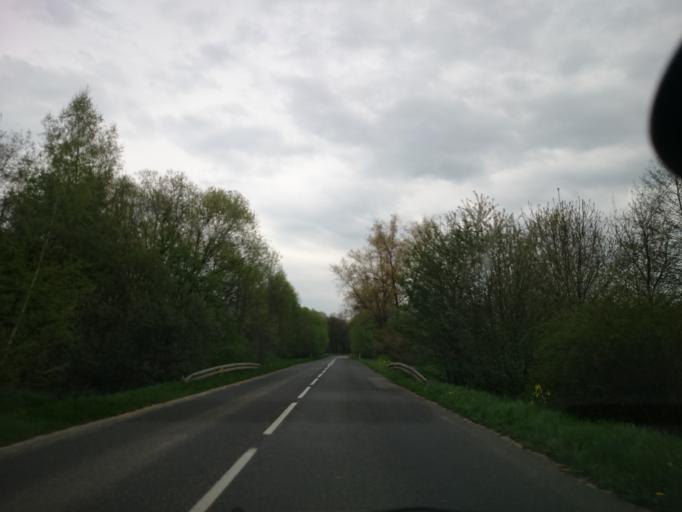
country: PL
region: Opole Voivodeship
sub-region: Powiat nyski
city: Glucholazy
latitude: 50.3818
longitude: 17.3553
